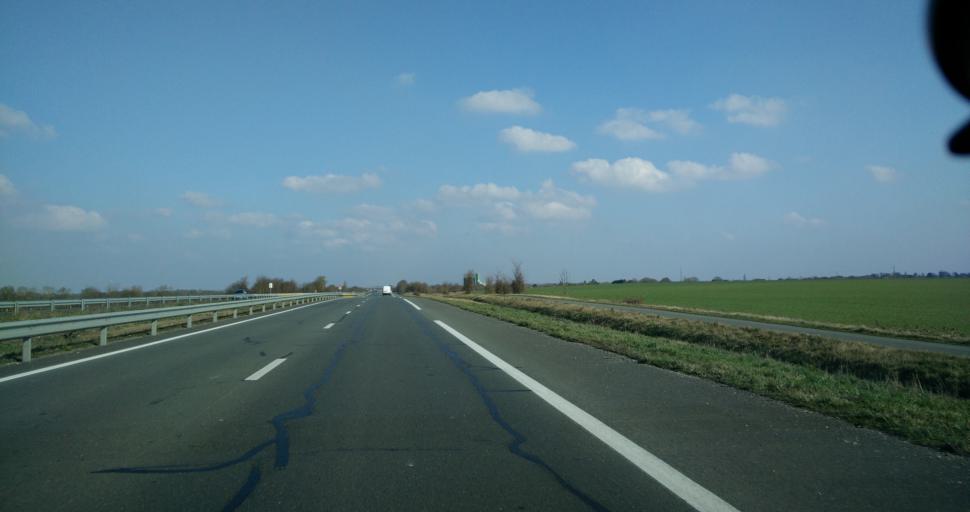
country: FR
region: Poitou-Charentes
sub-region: Departement de la Charente-Maritime
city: Sainte-Soulle
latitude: 46.2088
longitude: -1.0074
